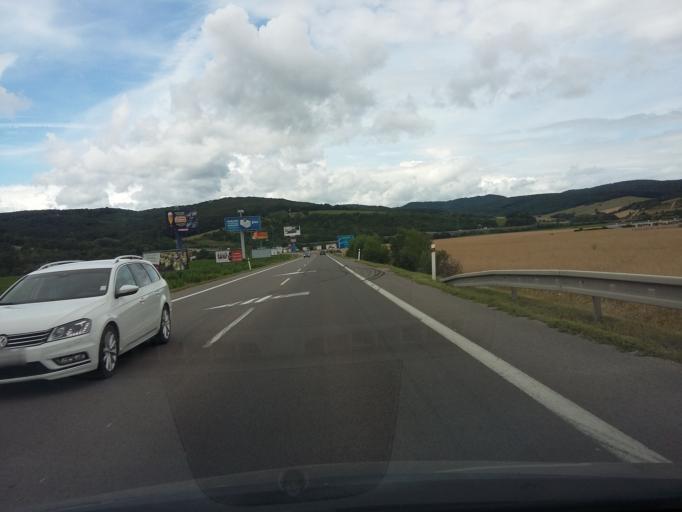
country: SK
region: Trenciansky
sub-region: Okres Trencin
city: Trencin
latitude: 48.8979
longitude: 17.9998
